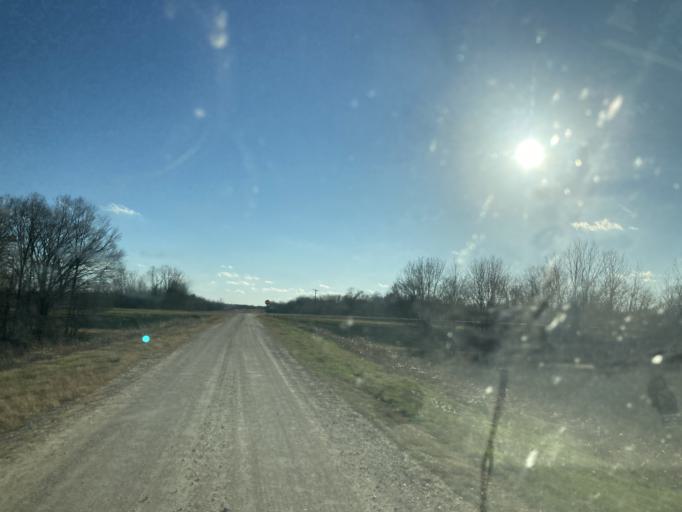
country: US
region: Mississippi
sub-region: Yazoo County
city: Yazoo City
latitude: 32.9179
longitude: -90.5542
